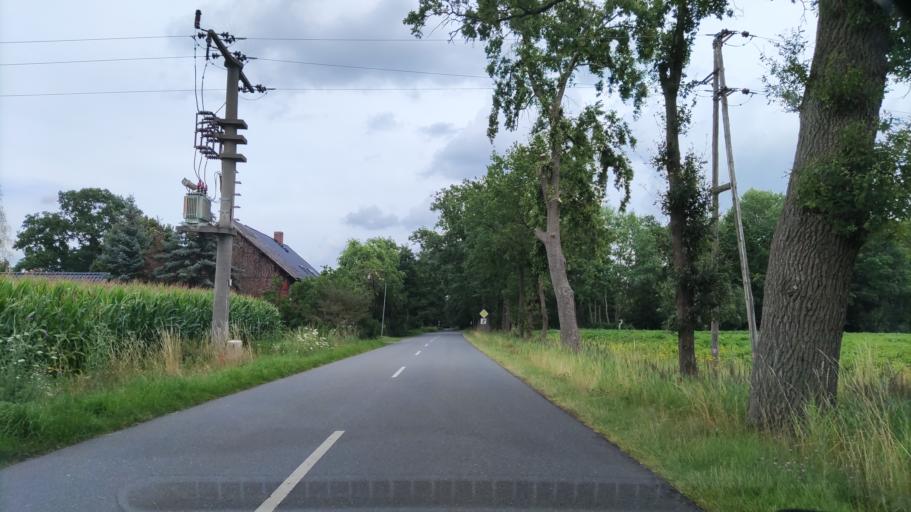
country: DE
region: Lower Saxony
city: Jameln
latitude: 53.0541
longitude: 11.1385
